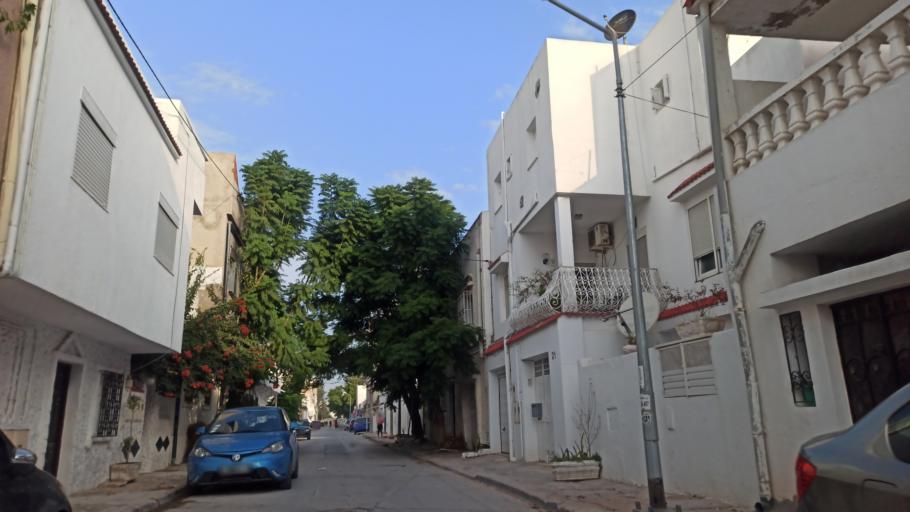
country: TN
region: Tunis
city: La Goulette
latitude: 36.8522
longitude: 10.2653
